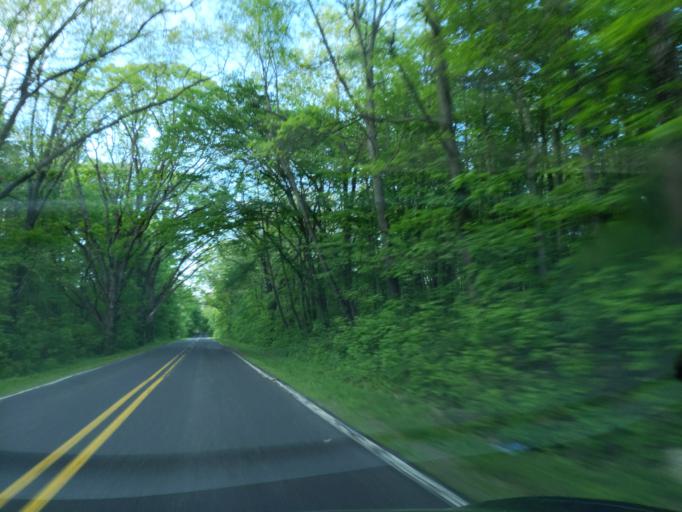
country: US
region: Michigan
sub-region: Ingham County
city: Stockbridge
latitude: 42.5186
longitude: -84.3049
